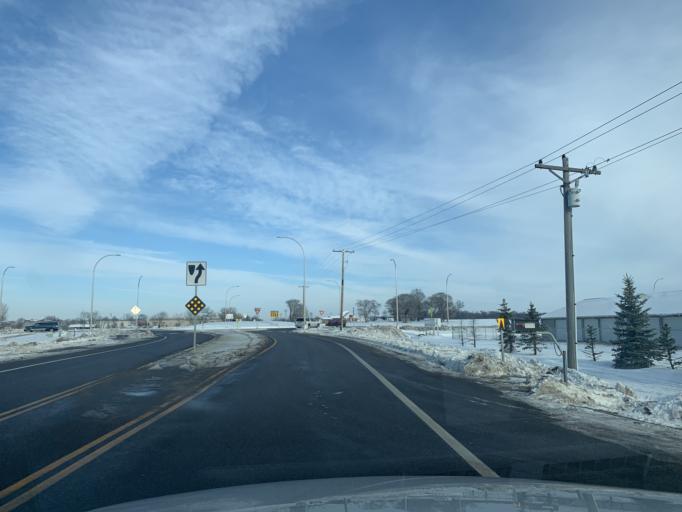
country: US
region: Minnesota
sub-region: Wright County
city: Buffalo
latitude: 45.1646
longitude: -93.8474
